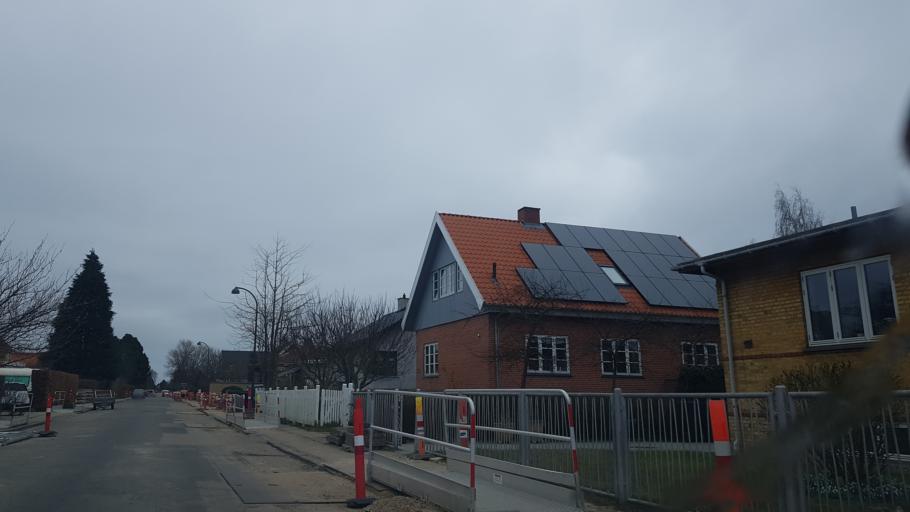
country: DK
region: Capital Region
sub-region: Gladsaxe Municipality
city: Buddinge
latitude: 55.7485
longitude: 12.5019
